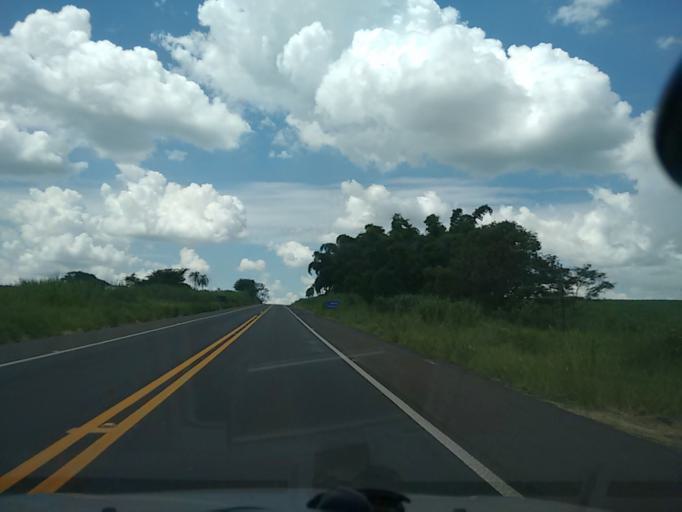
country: BR
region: Sao Paulo
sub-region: Osvaldo Cruz
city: Osvaldo Cruz
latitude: -21.8466
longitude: -50.8333
